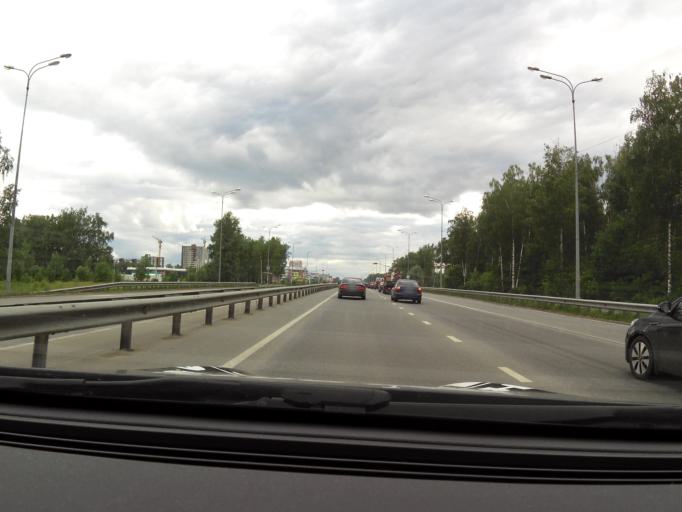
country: RU
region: Tatarstan
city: Osinovo
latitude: 55.8466
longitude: 48.9196
